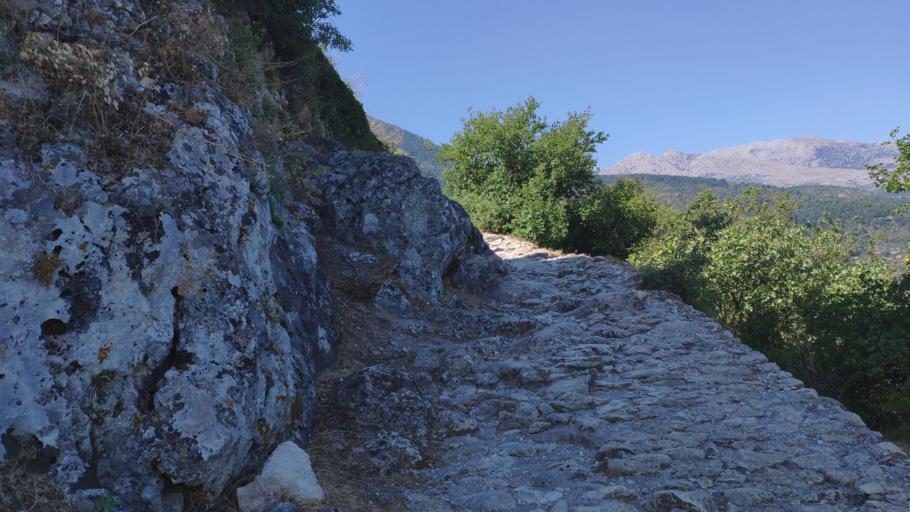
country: GR
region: Peloponnese
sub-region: Nomos Lakonias
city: Magoula
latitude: 37.0723
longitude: 22.3670
